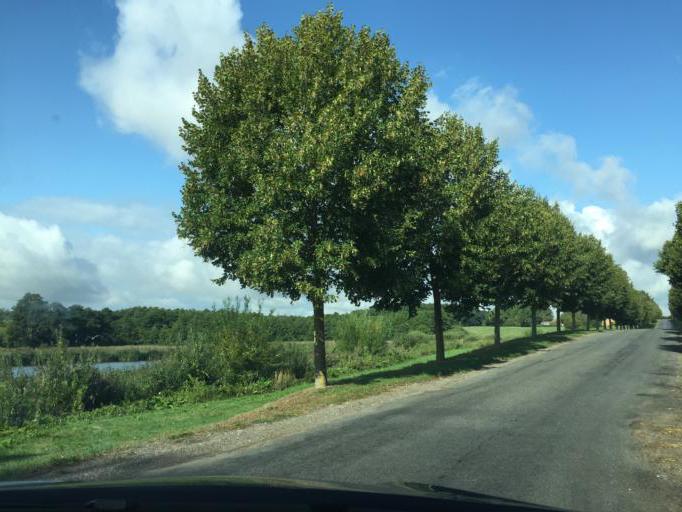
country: DK
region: South Denmark
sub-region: Faaborg-Midtfyn Kommune
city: Faaborg
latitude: 55.1942
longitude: 10.2777
